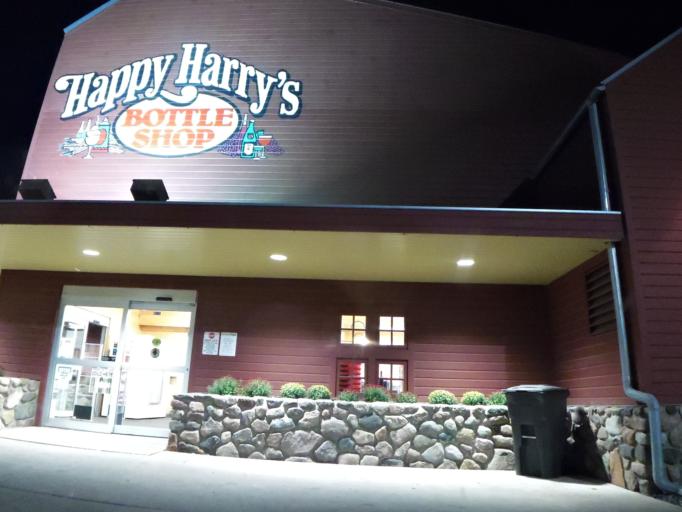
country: US
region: North Dakota
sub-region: Grand Forks County
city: Grand Forks
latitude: 47.8888
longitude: -97.0567
